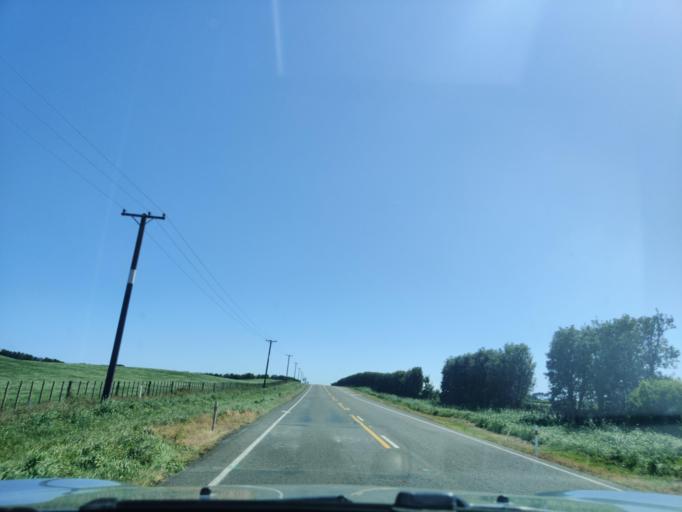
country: NZ
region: Taranaki
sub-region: South Taranaki District
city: Patea
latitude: -39.6980
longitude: 174.4328
